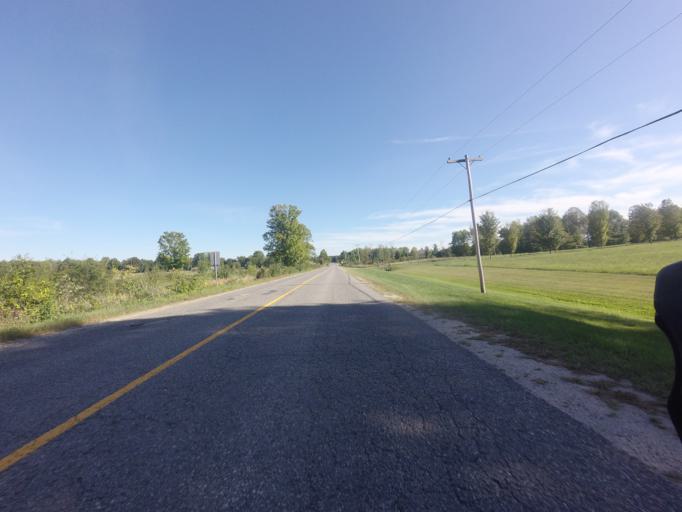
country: CA
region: Ontario
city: Perth
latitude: 44.9158
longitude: -76.3513
